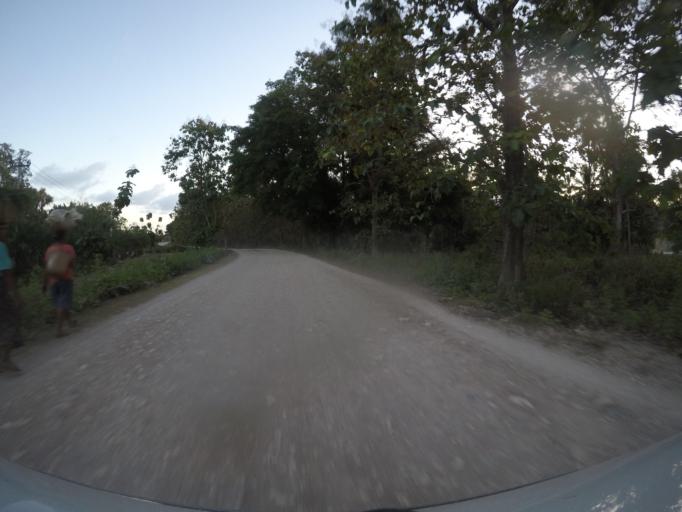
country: TL
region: Viqueque
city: Viqueque
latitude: -8.7681
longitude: 126.6437
